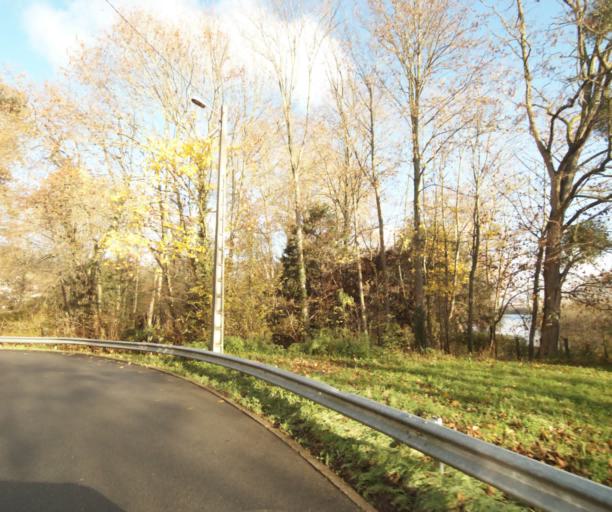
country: FR
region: Ile-de-France
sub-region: Departement des Yvelines
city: Meulan-en-Yvelines
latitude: 49.0040
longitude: 1.9162
